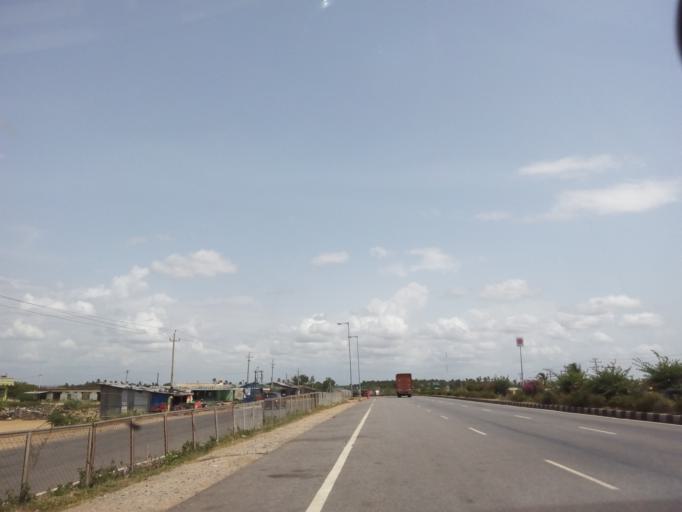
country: IN
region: Karnataka
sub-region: Tumkur
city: Sira
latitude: 13.7054
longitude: 76.9146
